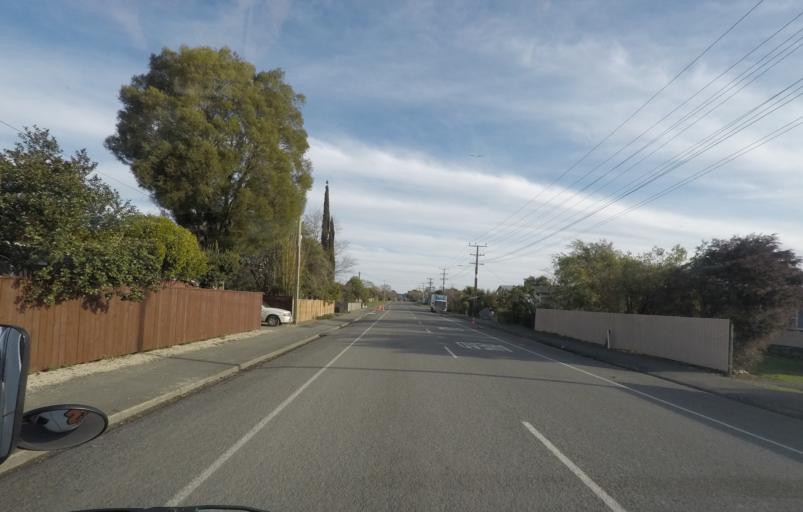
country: NZ
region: Tasman
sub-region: Tasman District
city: Brightwater
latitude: -41.3745
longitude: 173.1063
